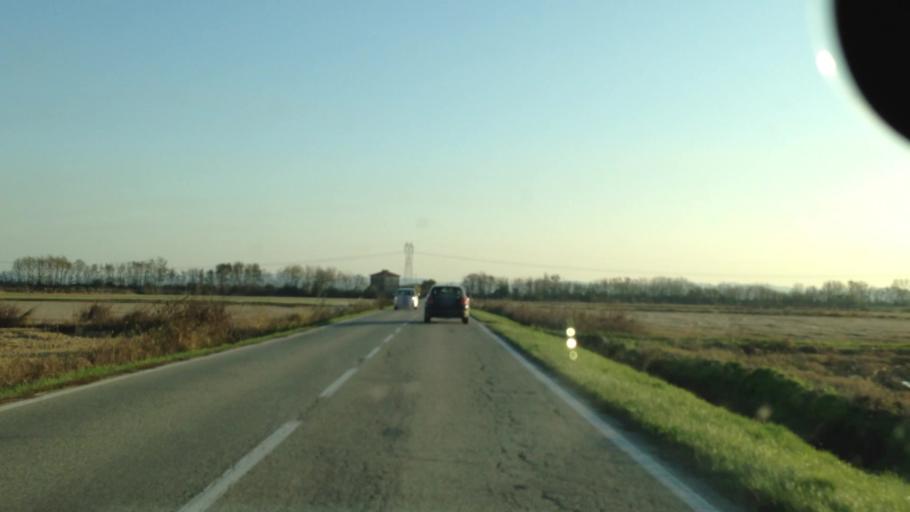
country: IT
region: Piedmont
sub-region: Provincia di Vercelli
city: Lamporo
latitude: 45.2494
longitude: 8.0889
